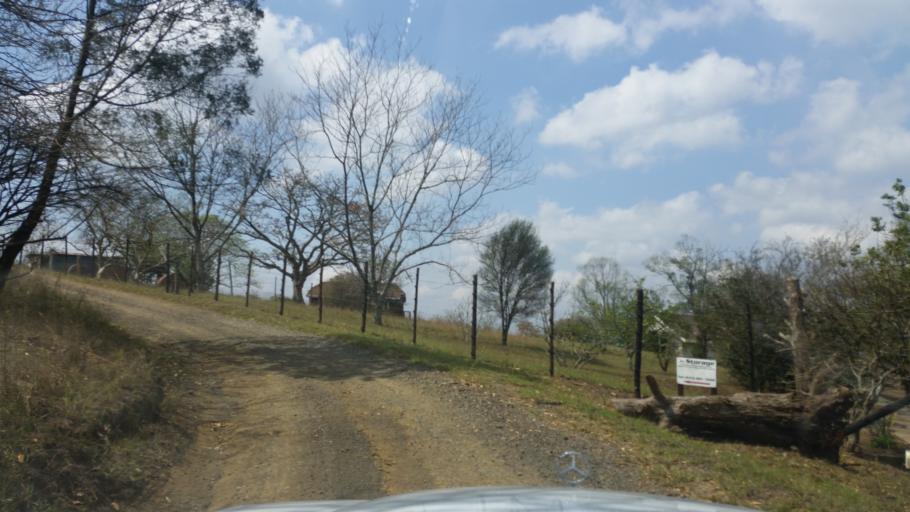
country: ZA
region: KwaZulu-Natal
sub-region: uMgungundlovu District Municipality
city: Camperdown
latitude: -29.7164
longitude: 30.5054
